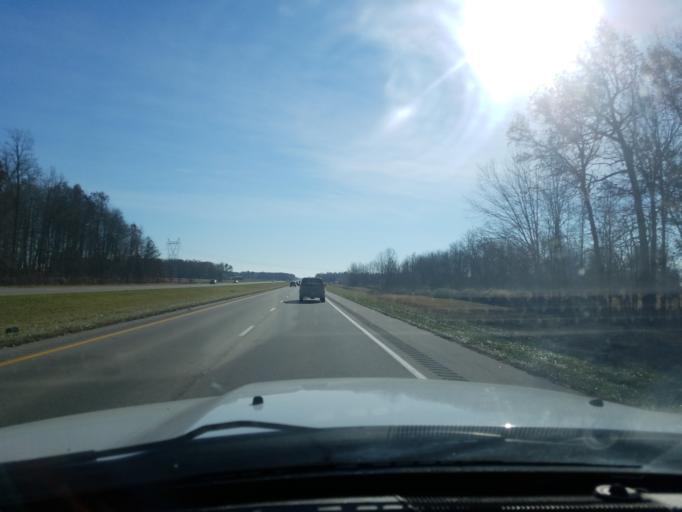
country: US
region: Ohio
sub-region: Brown County
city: Mount Orab
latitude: 39.0080
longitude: -83.7878
